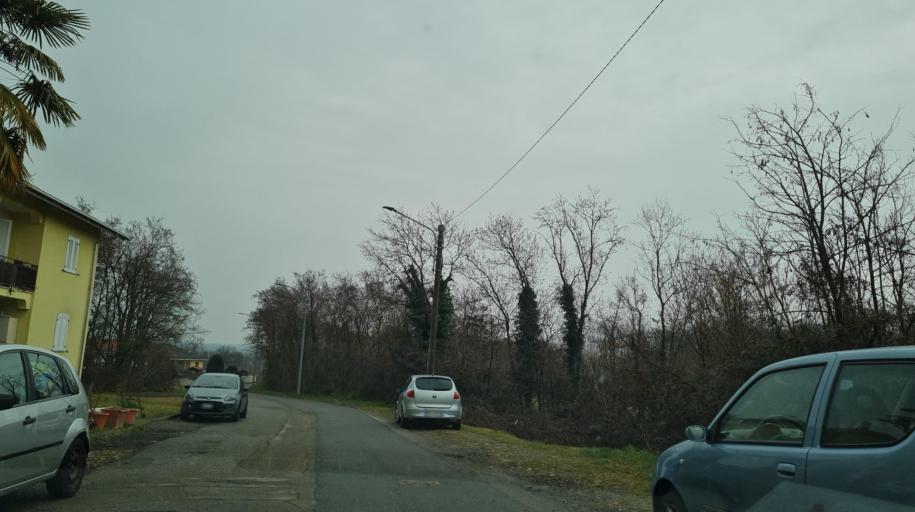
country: IT
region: Piedmont
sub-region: Provincia di Biella
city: Ceresane-Curanuova
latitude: 45.5125
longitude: 8.0065
